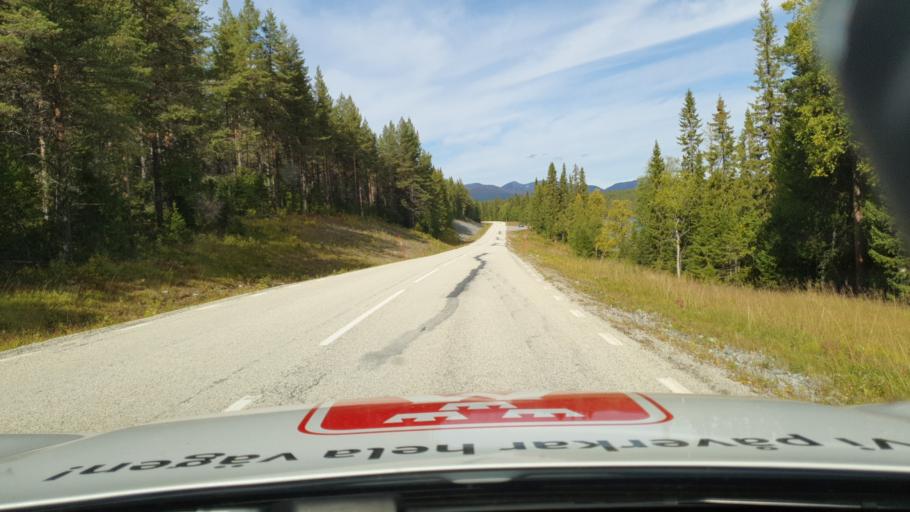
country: SE
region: Jaemtland
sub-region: Are Kommun
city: Are
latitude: 62.8347
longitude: 13.1932
